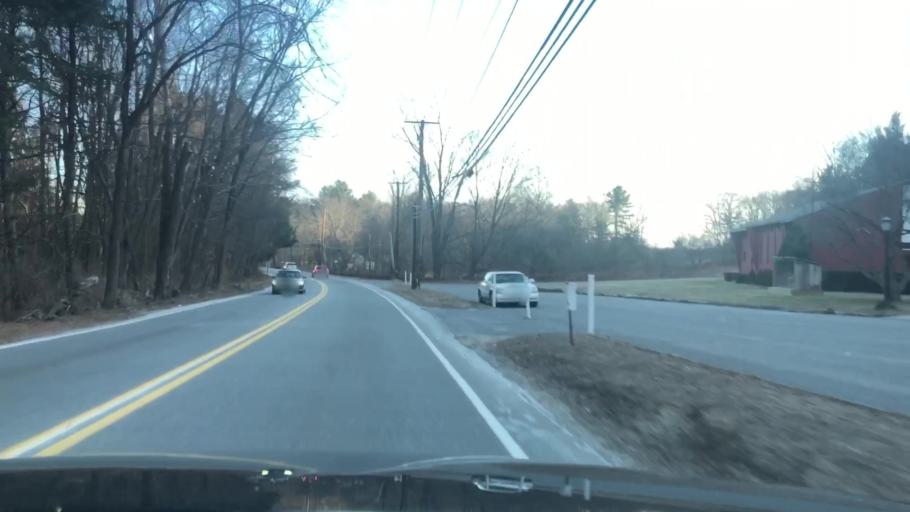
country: US
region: Massachusetts
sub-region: Worcester County
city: Bolton
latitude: 42.4378
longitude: -71.6166
